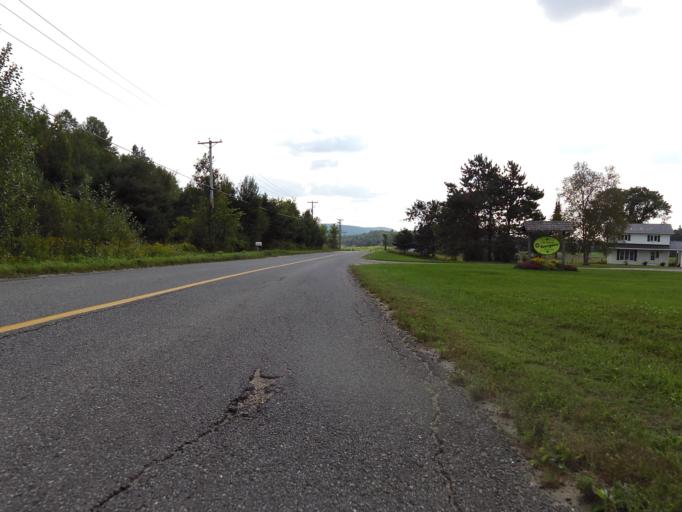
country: CA
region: Quebec
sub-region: Outaouais
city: Wakefield
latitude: 45.6667
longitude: -76.0140
